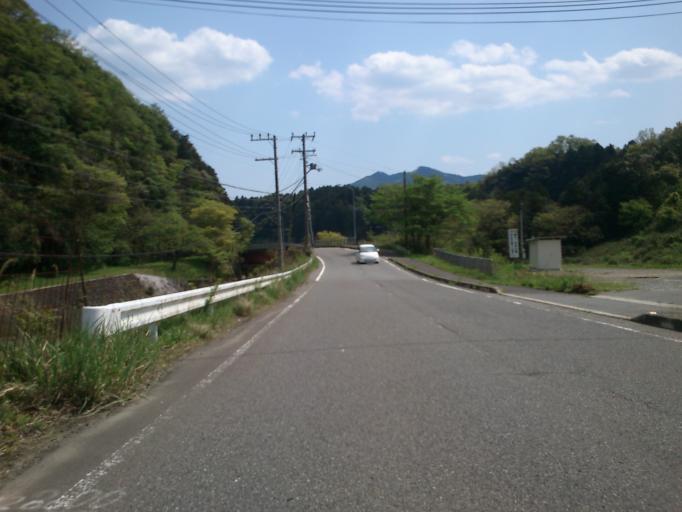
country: JP
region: Kyoto
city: Fukuchiyama
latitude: 35.3407
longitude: 134.9376
